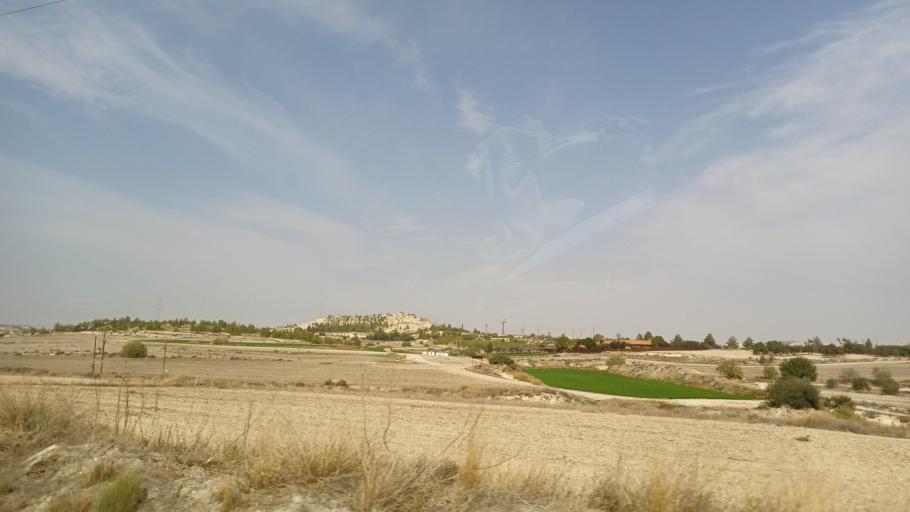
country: CY
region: Larnaka
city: Aradippou
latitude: 34.9646
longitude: 33.5494
